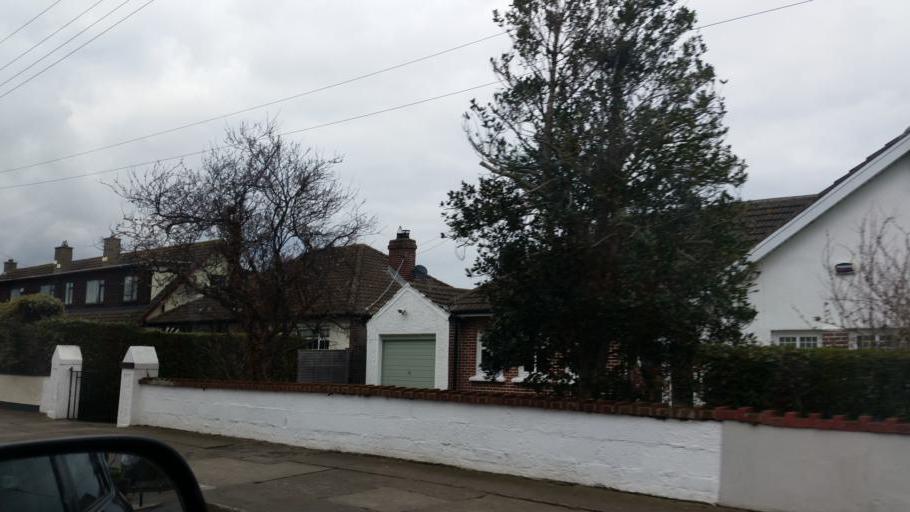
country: IE
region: Leinster
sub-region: Fingal County
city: Baldoyle
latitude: 53.3963
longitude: -6.1317
